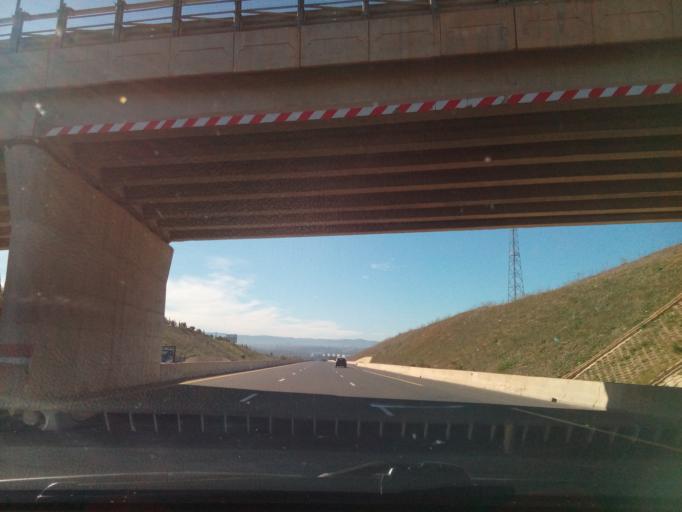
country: DZ
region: Tlemcen
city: Chetouane
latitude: 34.9695
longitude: -1.2642
